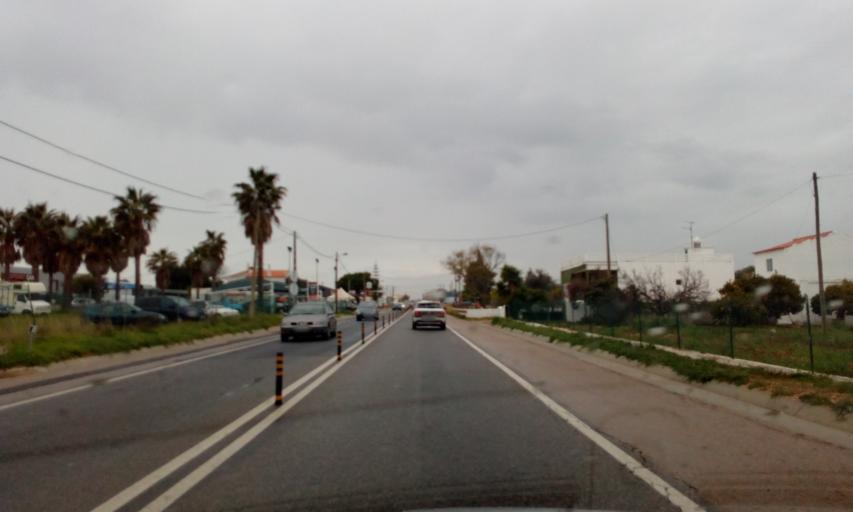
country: PT
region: Faro
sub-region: Albufeira
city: Guia
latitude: 37.1286
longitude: -8.2690
